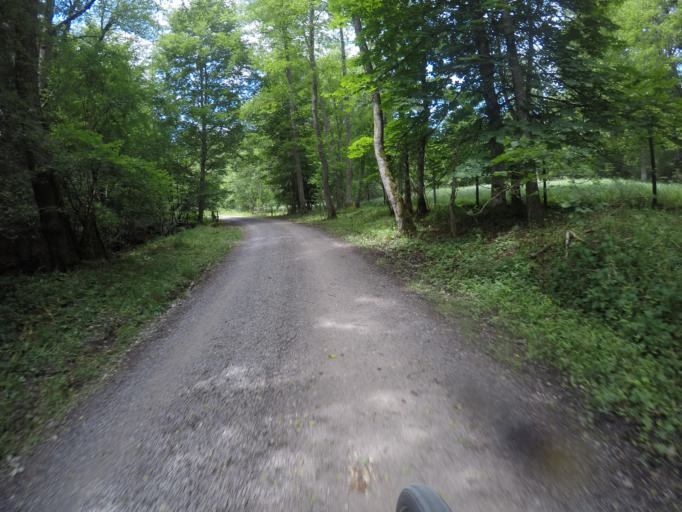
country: DE
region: Baden-Wuerttemberg
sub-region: Regierungsbezirk Stuttgart
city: Hildrizhausen
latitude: 48.5955
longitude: 8.9771
